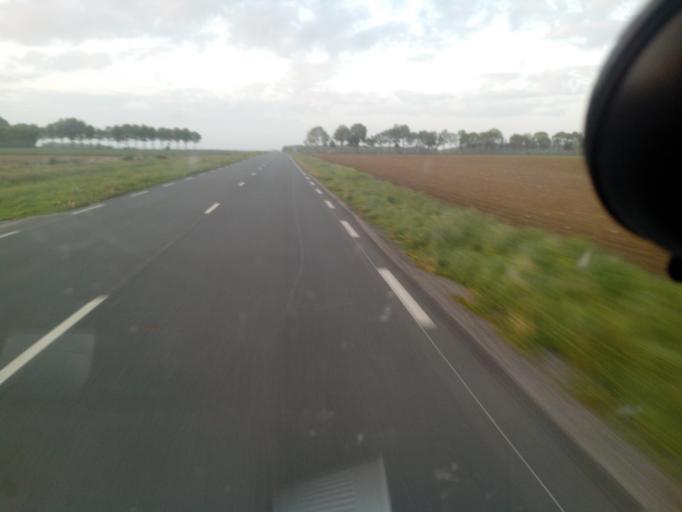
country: FR
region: Picardie
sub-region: Departement de la Somme
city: Crecy-en-Ponthieu
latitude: 50.2047
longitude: 1.8984
